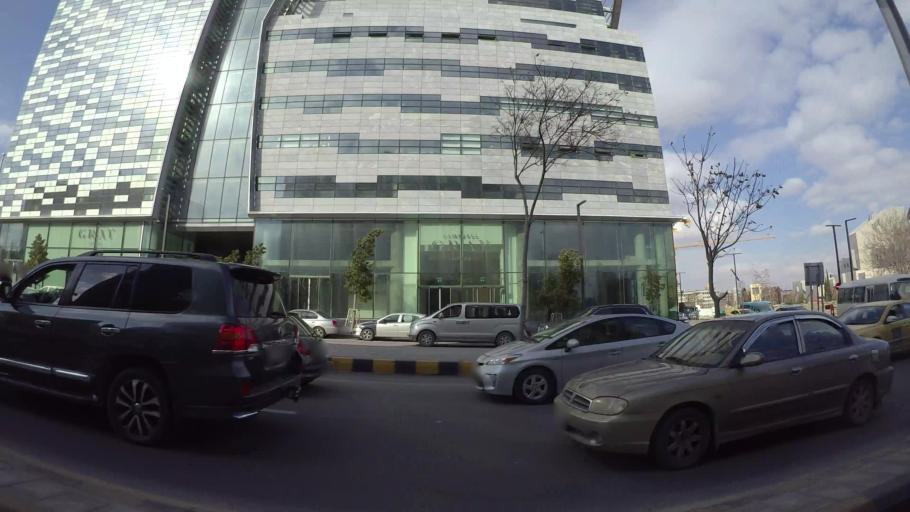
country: JO
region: Amman
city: Amman
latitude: 31.9617
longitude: 35.9083
